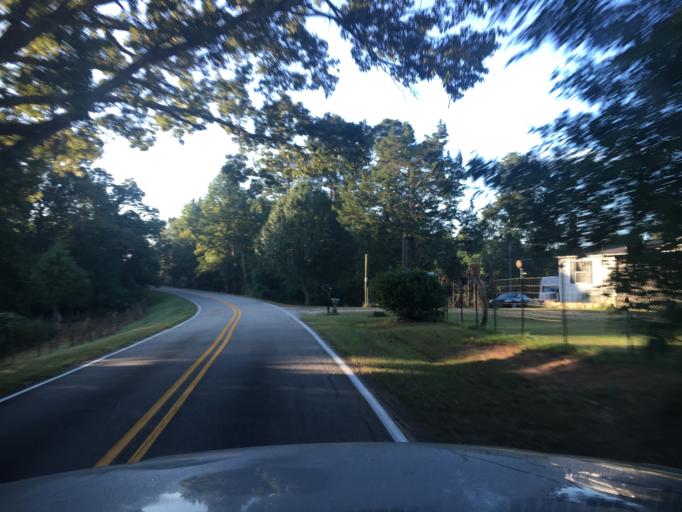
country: US
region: South Carolina
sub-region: Spartanburg County
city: Woodruff
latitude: 34.7809
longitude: -81.9854
